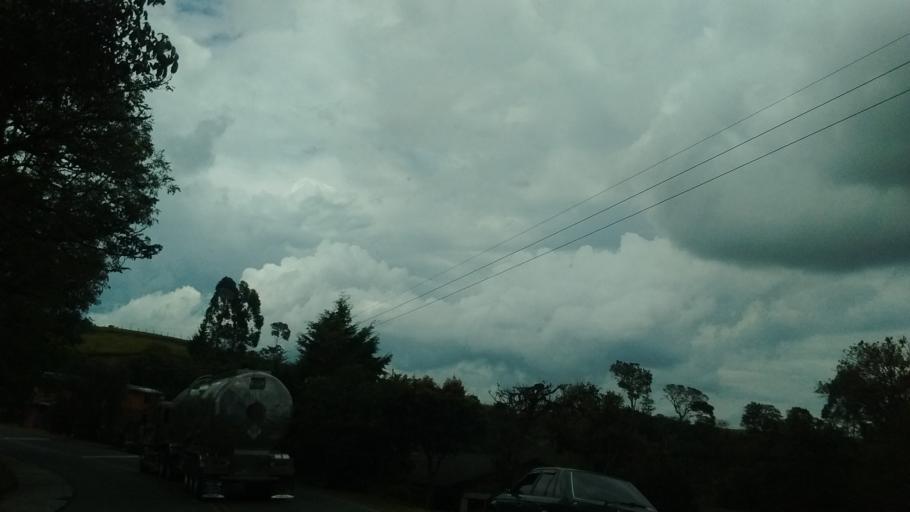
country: CO
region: Cauca
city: Rosas
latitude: 2.3285
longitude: -76.6931
